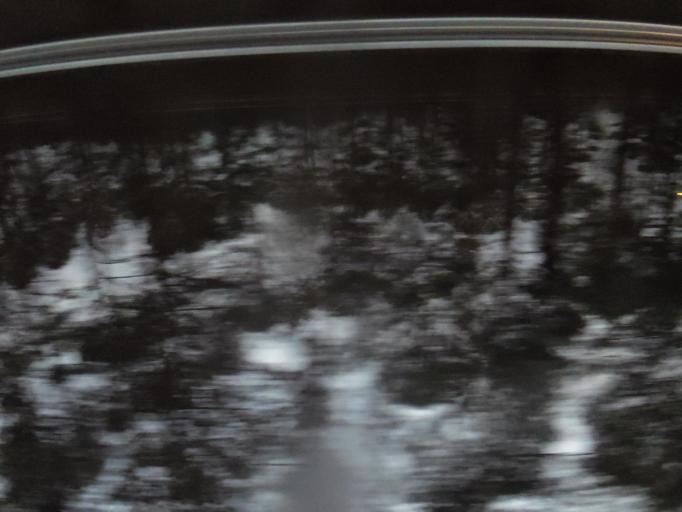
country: US
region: Alabama
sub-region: Cullman County
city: Cullman
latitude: 34.2092
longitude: -86.8794
